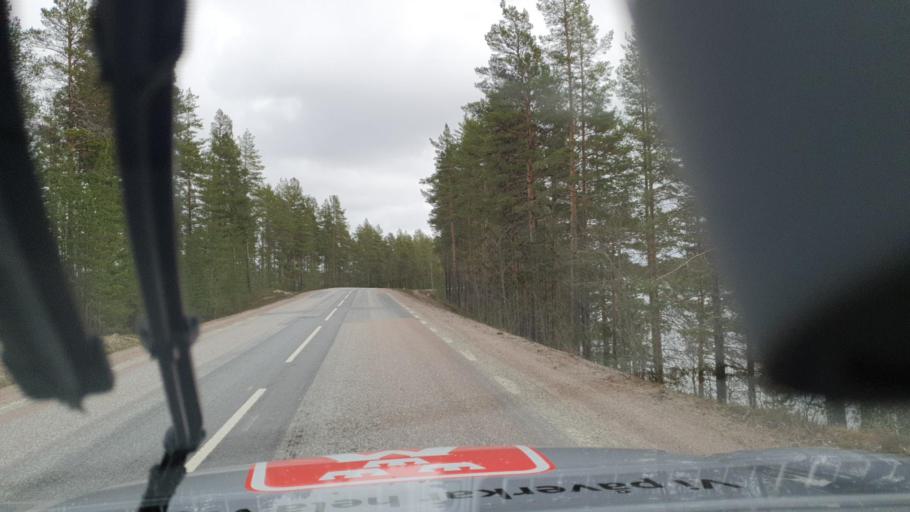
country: SE
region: Vaesternorrland
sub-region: Solleftea Kommun
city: Solleftea
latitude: 63.6494
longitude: 17.3702
